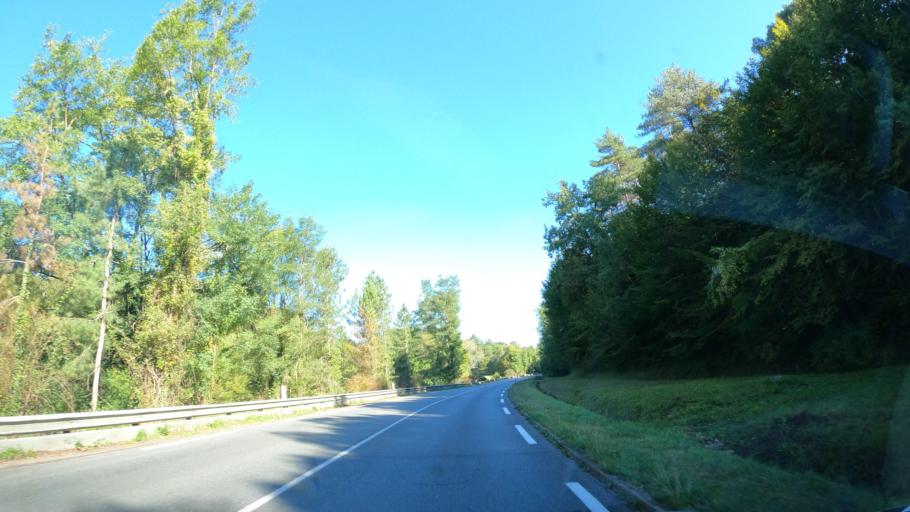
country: FR
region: Aquitaine
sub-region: Departement de la Dordogne
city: Notre-Dame-de-Sanilhac
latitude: 45.0869
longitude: 0.6893
